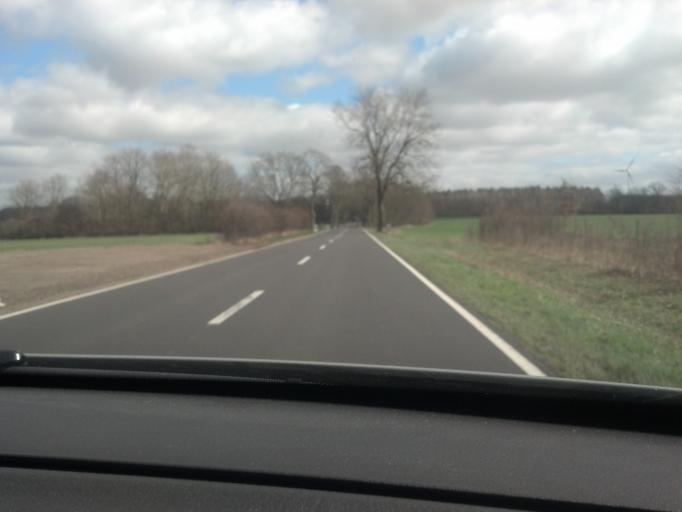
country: DE
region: Brandenburg
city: Gerdshagen
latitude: 53.2961
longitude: 12.1907
